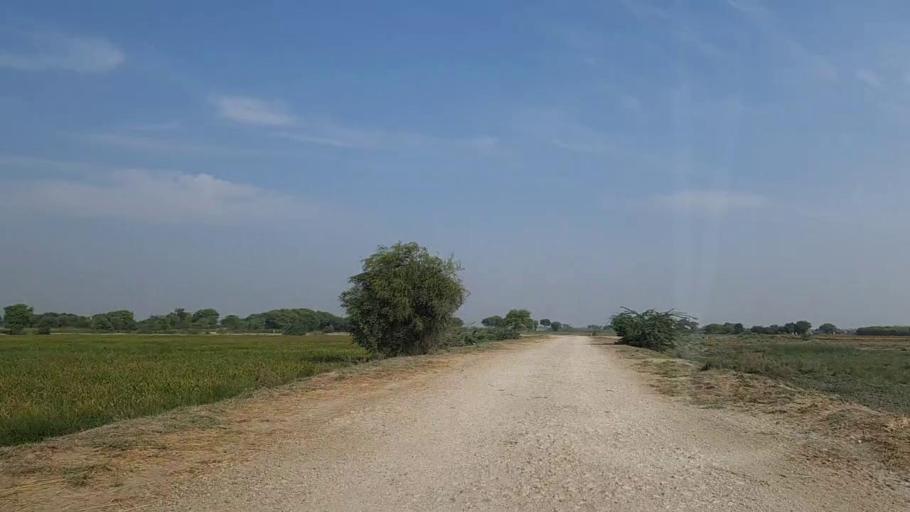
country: PK
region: Sindh
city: Mirpur Batoro
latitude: 24.7156
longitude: 68.2228
